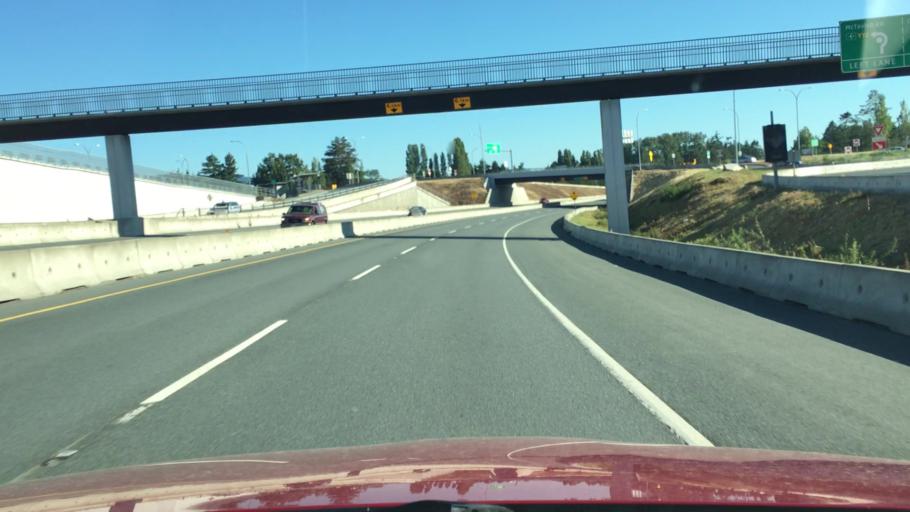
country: CA
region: British Columbia
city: North Saanich
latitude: 48.6289
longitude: -123.4119
